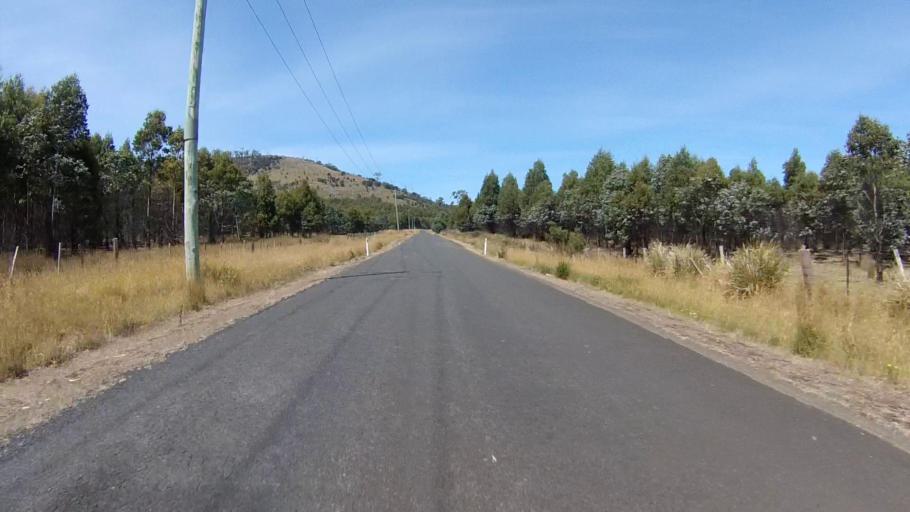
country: AU
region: Tasmania
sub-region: Sorell
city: Sorell
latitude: -42.6208
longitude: 147.7297
